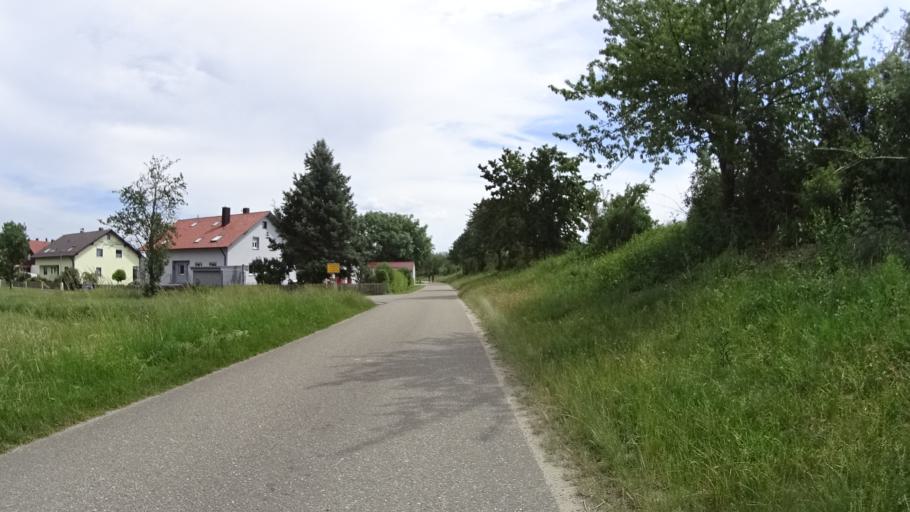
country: DE
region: Bavaria
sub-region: Upper Palatinate
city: Donaustauf
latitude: 49.0149
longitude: 12.2638
